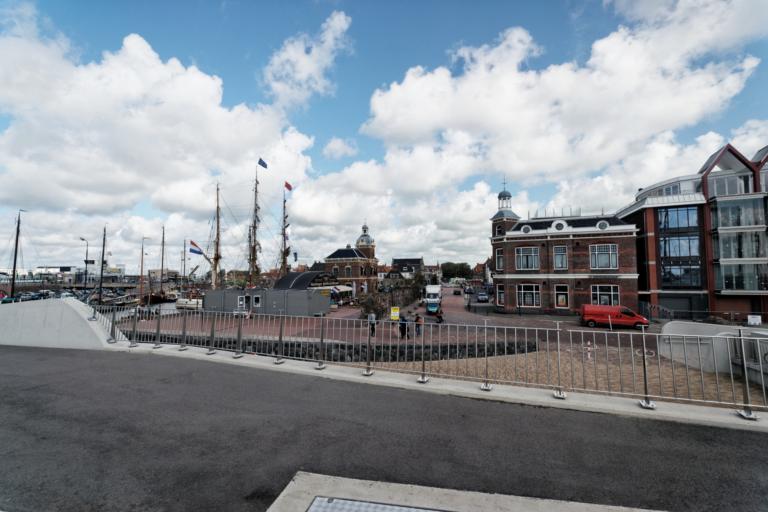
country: NL
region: Friesland
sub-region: Gemeente Harlingen
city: Harlingen
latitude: 53.1750
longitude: 5.4115
